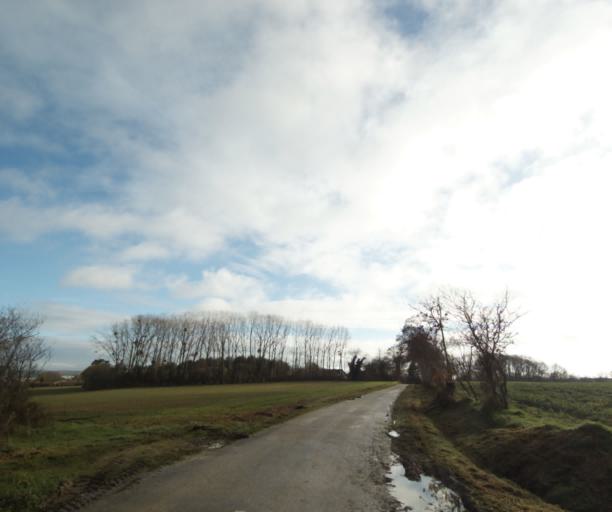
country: FR
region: Pays de la Loire
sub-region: Departement de la Sarthe
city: La Chapelle-Saint-Aubin
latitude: 48.0258
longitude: 0.1607
